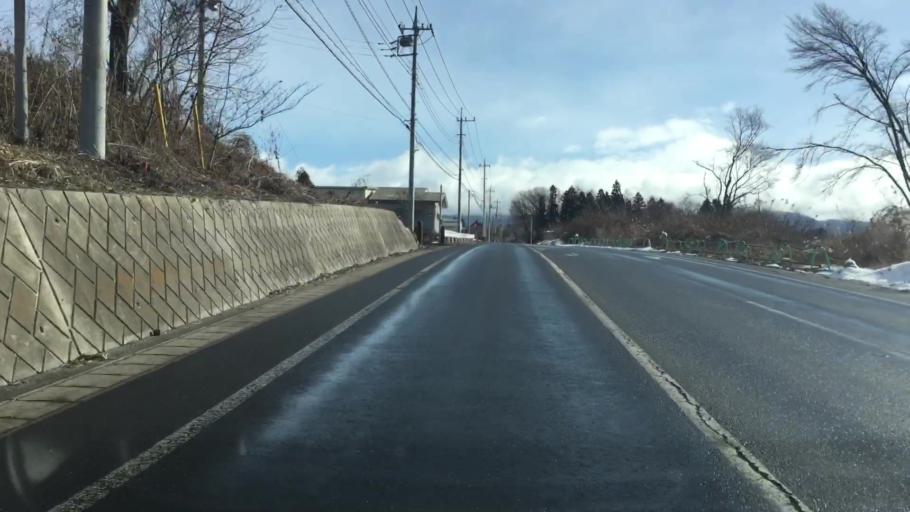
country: JP
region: Gunma
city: Numata
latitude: 36.6104
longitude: 139.0788
